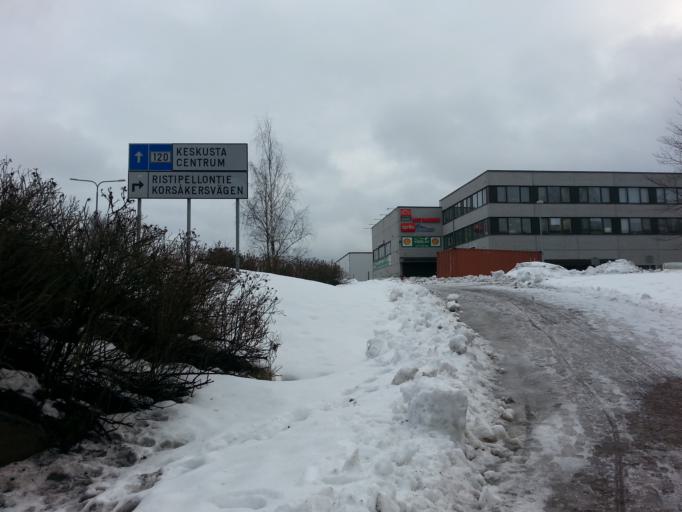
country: FI
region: Uusimaa
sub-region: Helsinki
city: Teekkarikylae
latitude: 60.2417
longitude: 24.8489
